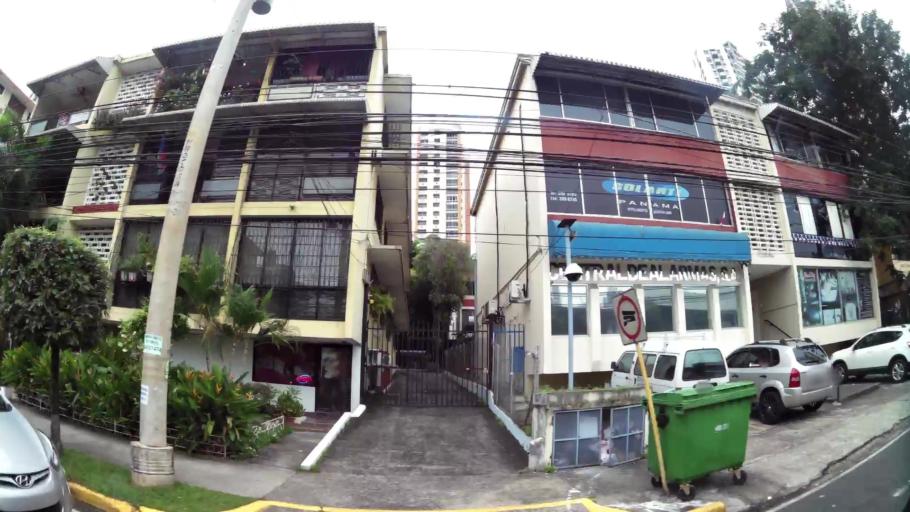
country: PA
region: Panama
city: Panama
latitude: 8.9860
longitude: -79.5277
